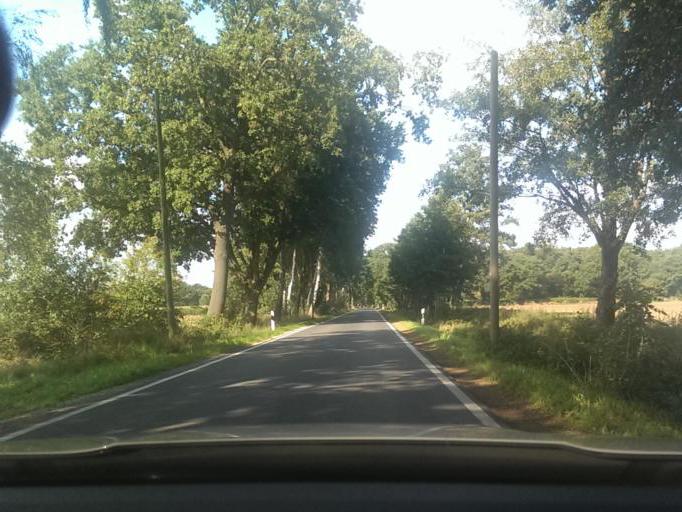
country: DE
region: Lower Saxony
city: Elze
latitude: 52.5421
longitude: 9.7628
